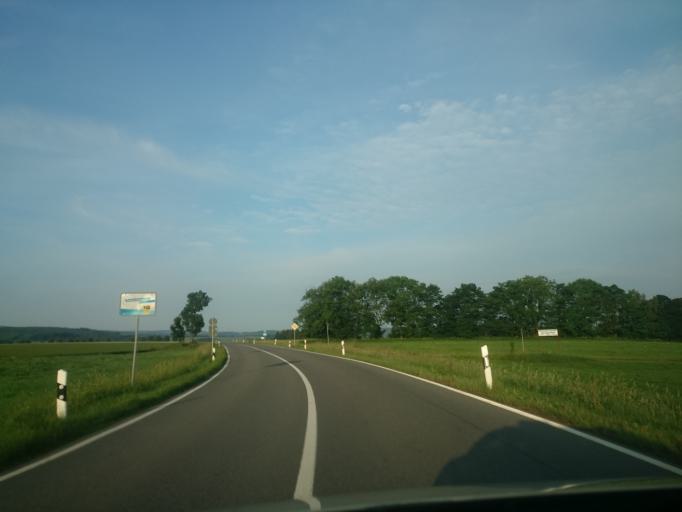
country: DE
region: Saxony
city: Pockau
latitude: 50.7403
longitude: 13.2806
